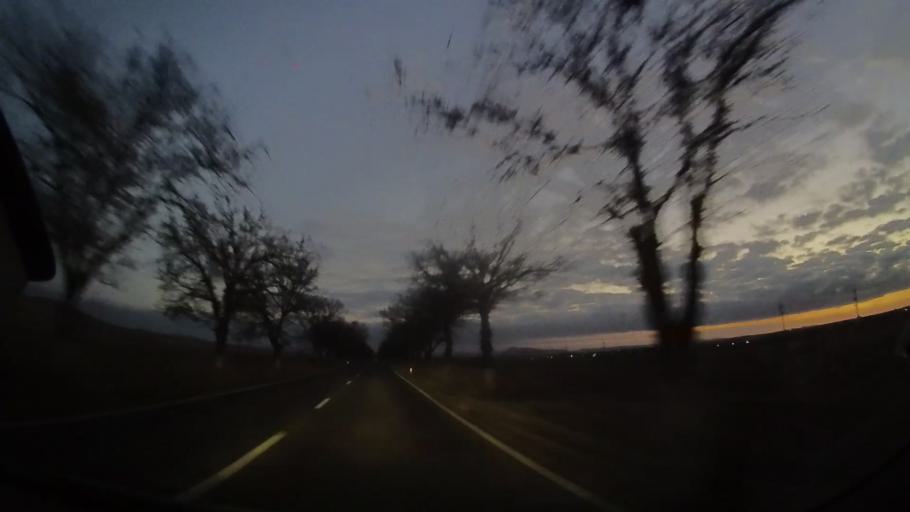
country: RO
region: Tulcea
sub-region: Comuna Frecatei
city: Cataloi
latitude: 45.1015
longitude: 28.7424
